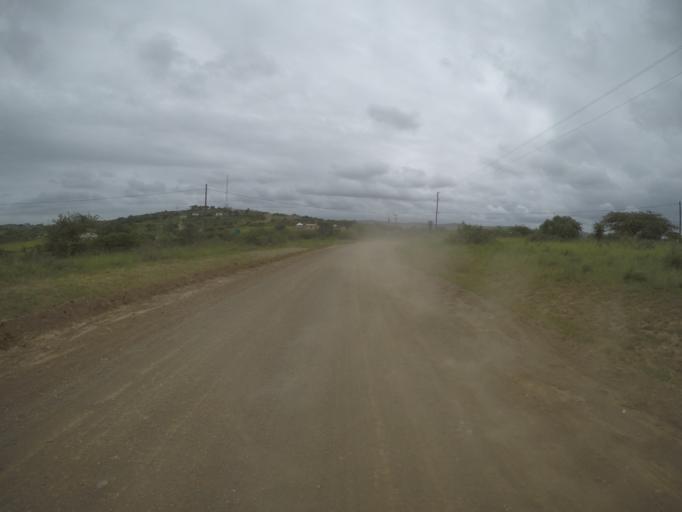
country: ZA
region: KwaZulu-Natal
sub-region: uThungulu District Municipality
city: Empangeni
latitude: -28.6027
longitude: 31.8401
